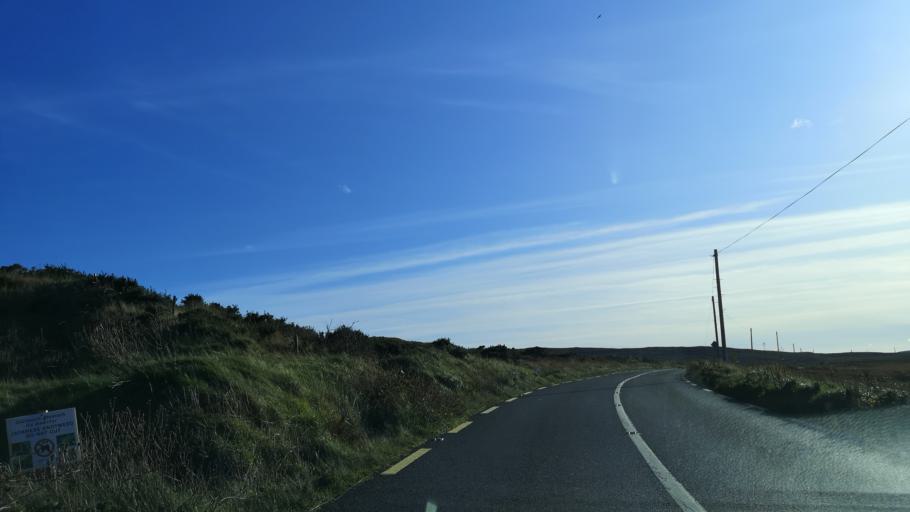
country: IE
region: Connaught
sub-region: County Galway
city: Clifden
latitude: 53.5400
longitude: -10.0298
